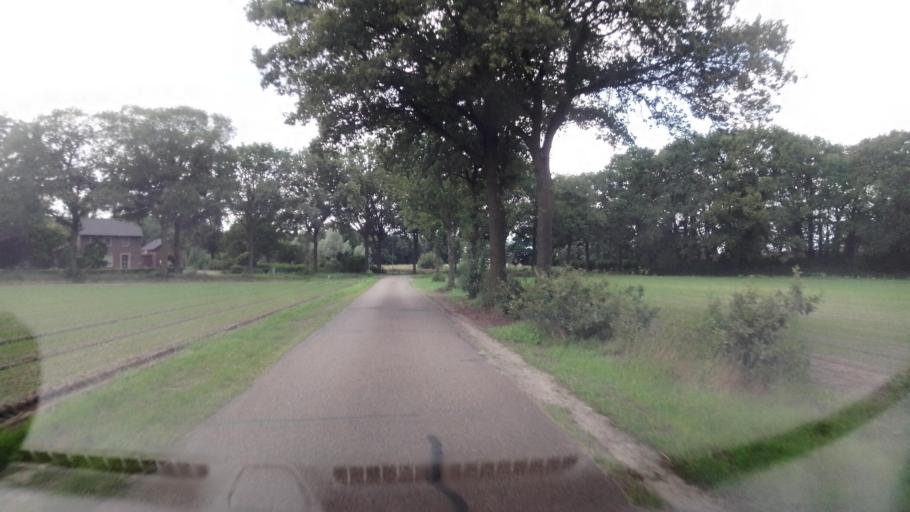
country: NL
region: Limburg
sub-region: Gemeente Peel en Maas
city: Maasbree
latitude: 51.3571
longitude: 6.0199
